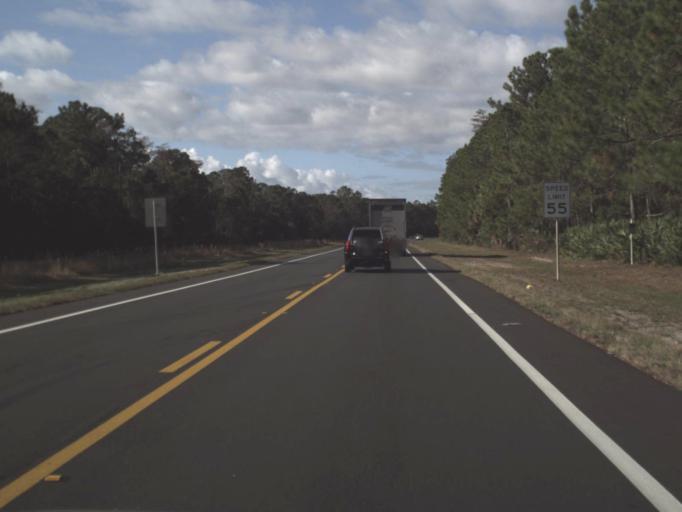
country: US
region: Florida
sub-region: Volusia County
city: South Daytona
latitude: 29.1378
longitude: -81.0543
